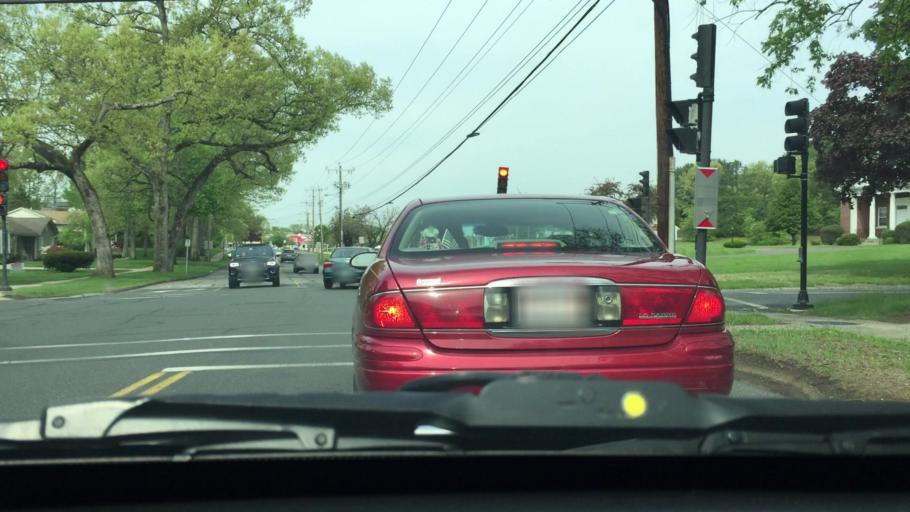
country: US
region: Massachusetts
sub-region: Hampden County
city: Longmeadow
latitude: 42.0565
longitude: -72.5500
